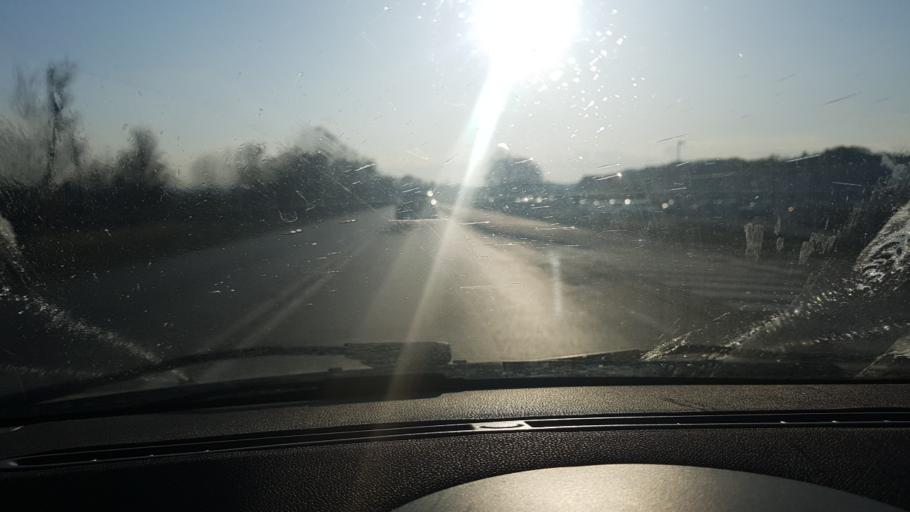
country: HR
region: Krapinsko-Zagorska
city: Zabok
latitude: 46.0187
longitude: 15.8987
